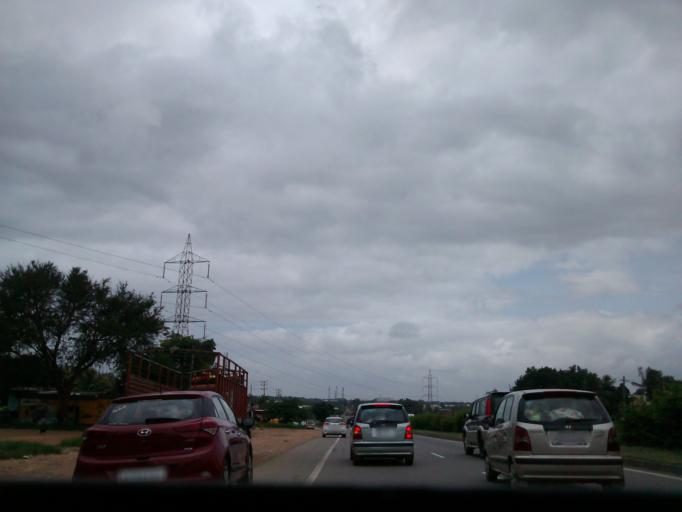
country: IN
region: Karnataka
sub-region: Bangalore Rural
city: Nelamangala
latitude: 13.1392
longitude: 77.3509
